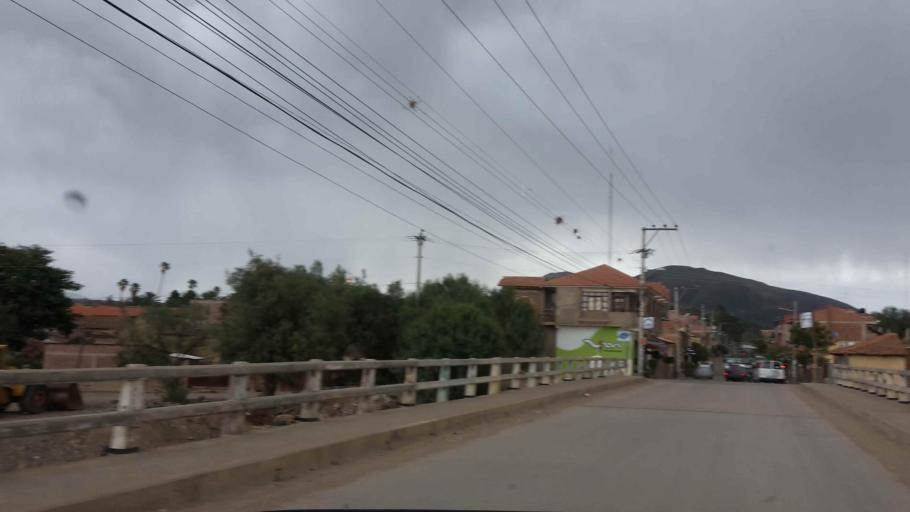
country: BO
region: Cochabamba
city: Tarata
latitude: -17.6108
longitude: -66.0206
